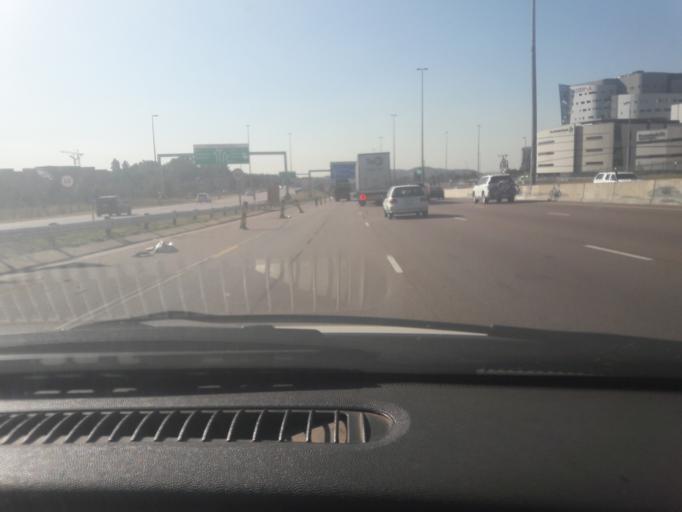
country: ZA
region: Gauteng
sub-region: City of Tshwane Metropolitan Municipality
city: Pretoria
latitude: -25.7880
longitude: 28.2693
